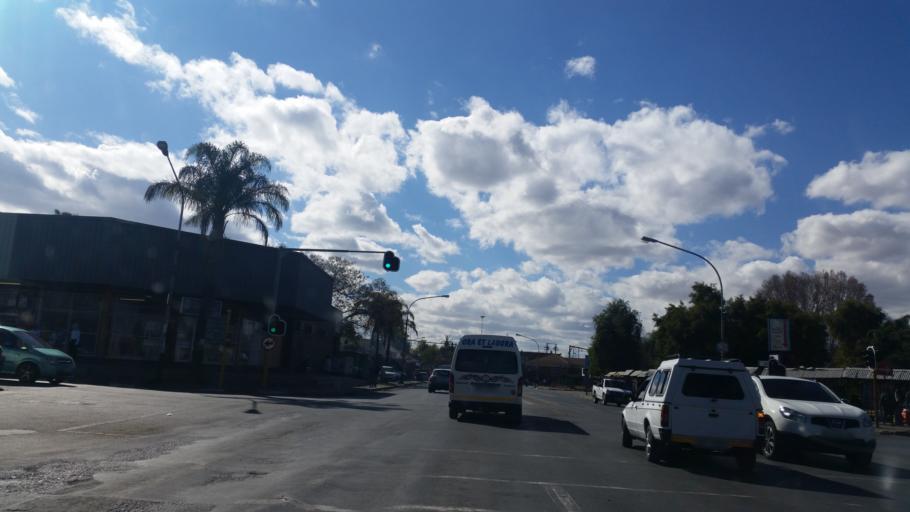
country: ZA
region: KwaZulu-Natal
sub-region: uThukela District Municipality
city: Ladysmith
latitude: -28.5586
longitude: 29.7843
